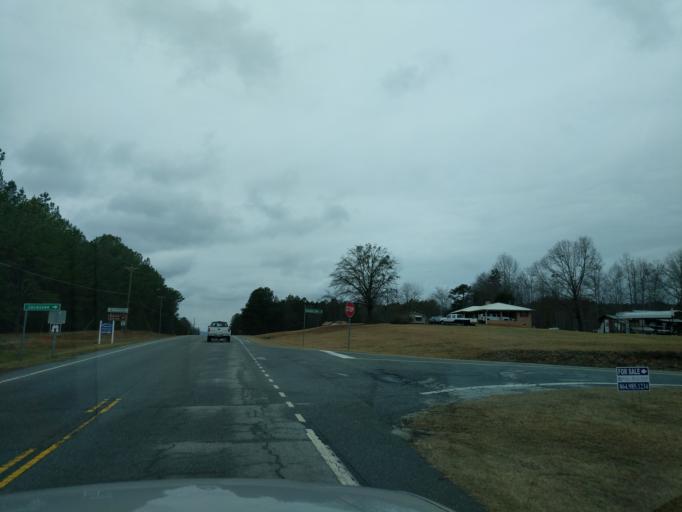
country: US
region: South Carolina
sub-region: Oconee County
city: Walhalla
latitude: 34.9098
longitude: -82.9582
